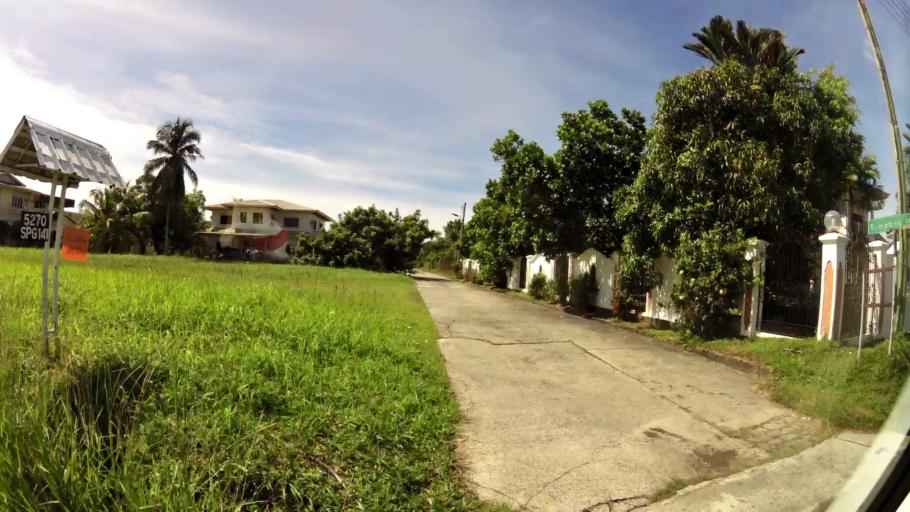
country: BN
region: Belait
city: Kuala Belait
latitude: 4.5874
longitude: 114.2165
